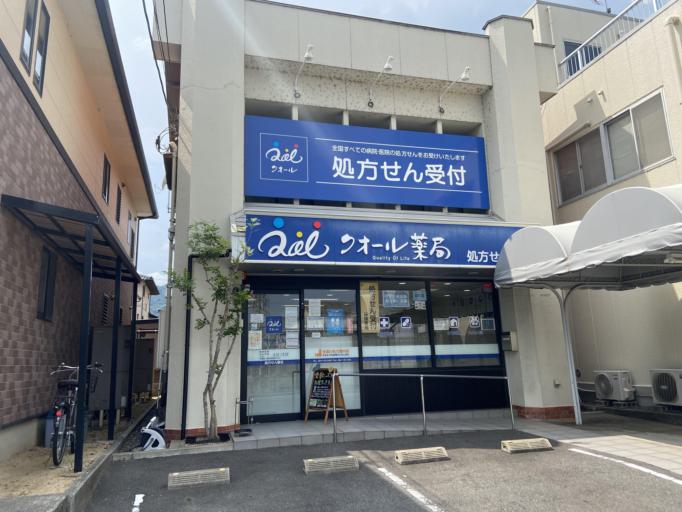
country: JP
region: Hiroshima
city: Fuchucho
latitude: 34.5687
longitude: 133.2415
